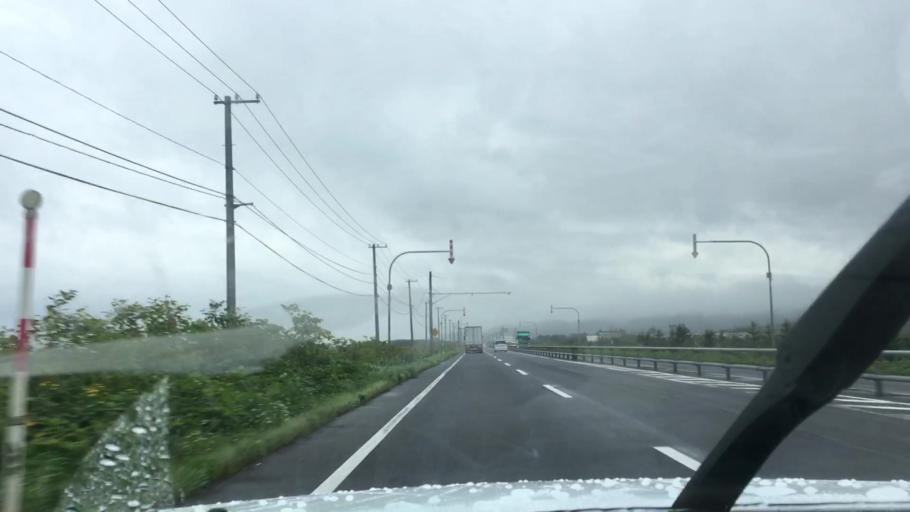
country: JP
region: Hokkaido
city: Niseko Town
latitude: 42.3999
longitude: 140.3029
